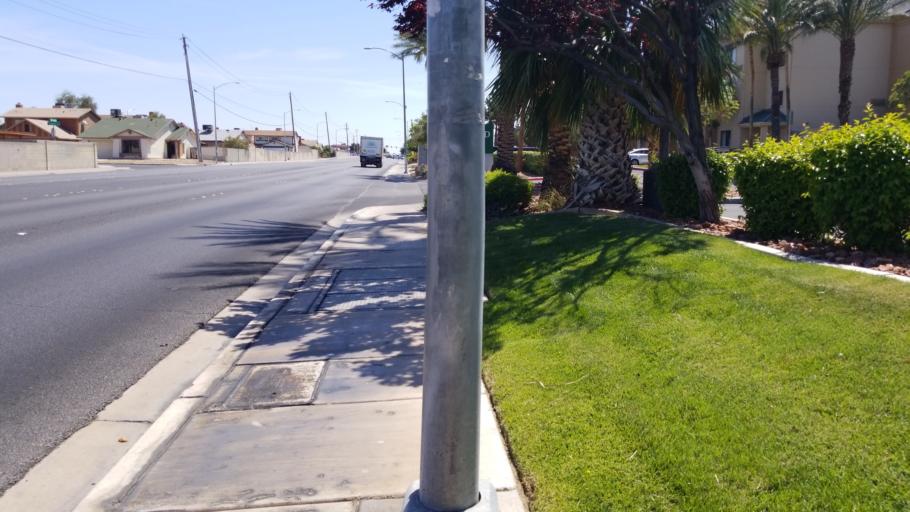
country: US
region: Nevada
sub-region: Clark County
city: Spring Valley
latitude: 36.1933
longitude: -115.2424
